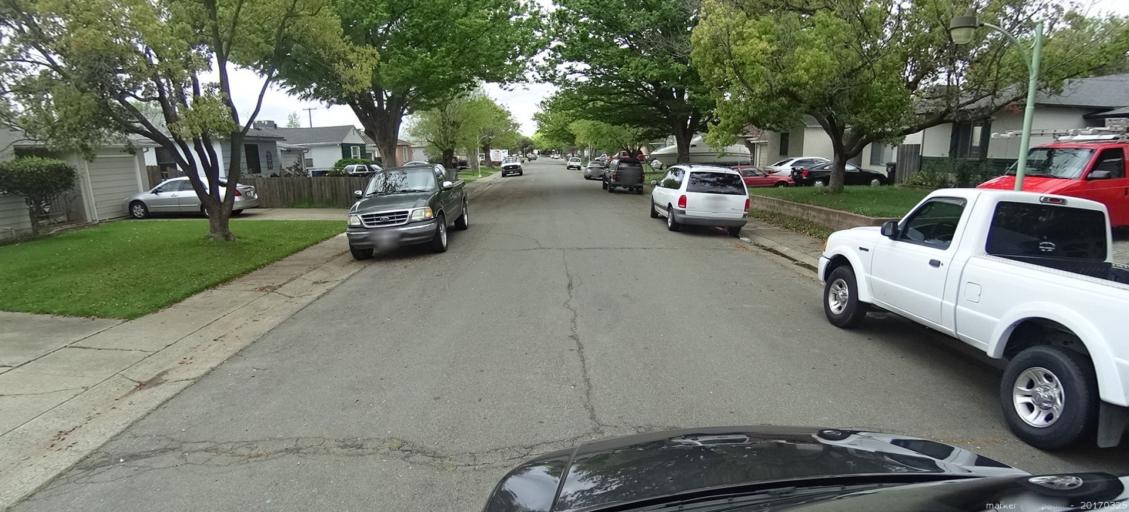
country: US
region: California
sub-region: Sacramento County
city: Parkway
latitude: 38.5188
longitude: -121.4342
